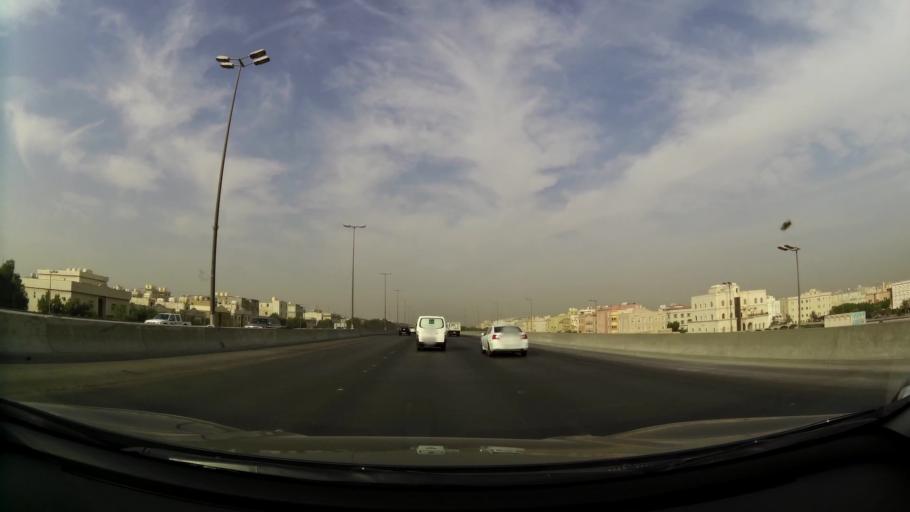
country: KW
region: Al Farwaniyah
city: Al Farwaniyah
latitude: 29.2668
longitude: 47.9401
